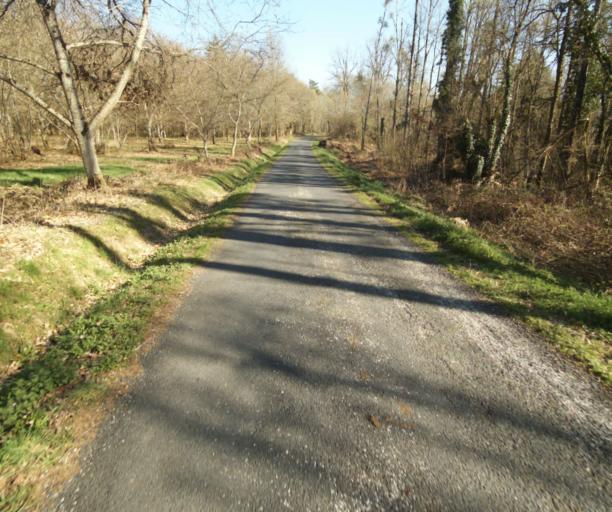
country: FR
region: Limousin
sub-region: Departement de la Correze
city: Chameyrat
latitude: 45.2893
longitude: 1.7059
